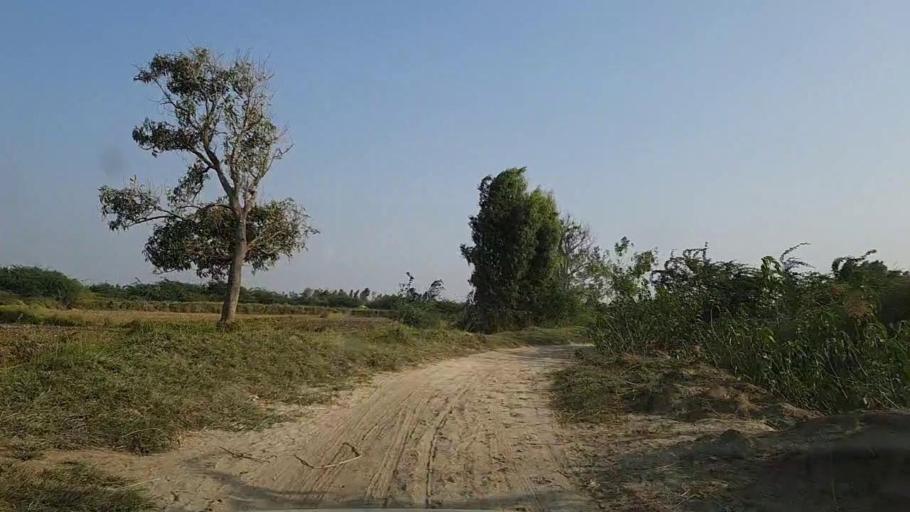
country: PK
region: Sindh
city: Mirpur Sakro
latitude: 24.5884
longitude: 67.6480
